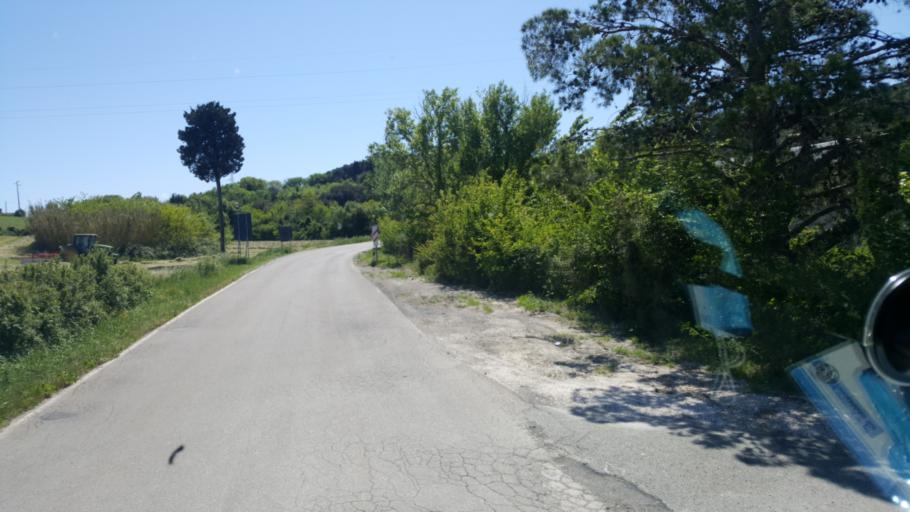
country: IT
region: Tuscany
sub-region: Provincia di Livorno
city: Rosignano Marittimo
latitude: 43.4090
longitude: 10.4976
